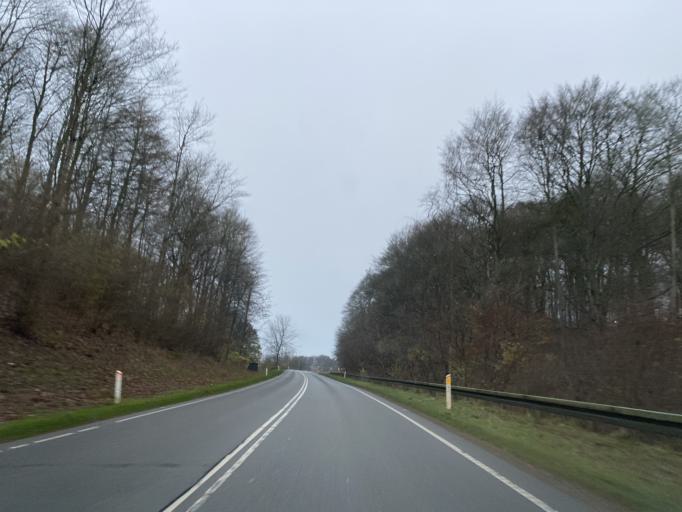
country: DK
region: Central Jutland
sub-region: Skanderborg Kommune
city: Skanderborg
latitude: 56.0286
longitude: 9.9621
